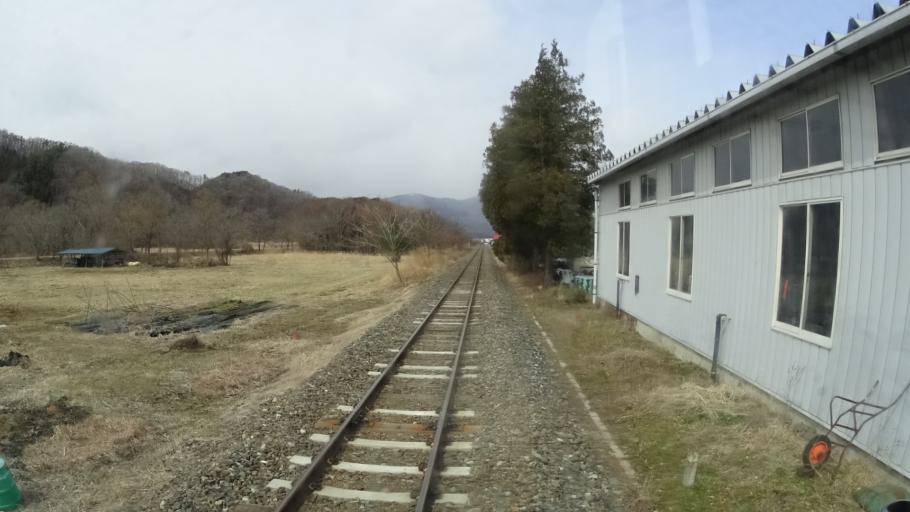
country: JP
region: Iwate
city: Tono
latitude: 39.3223
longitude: 141.5583
